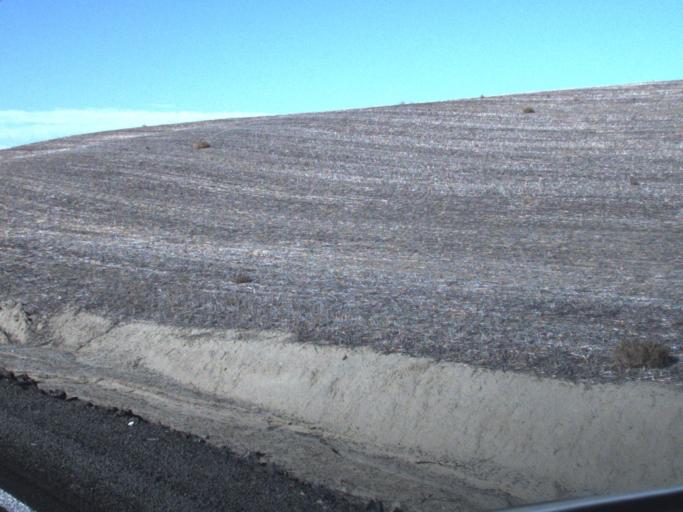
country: US
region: Washington
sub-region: Walla Walla County
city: Walla Walla
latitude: 46.1264
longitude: -118.3738
